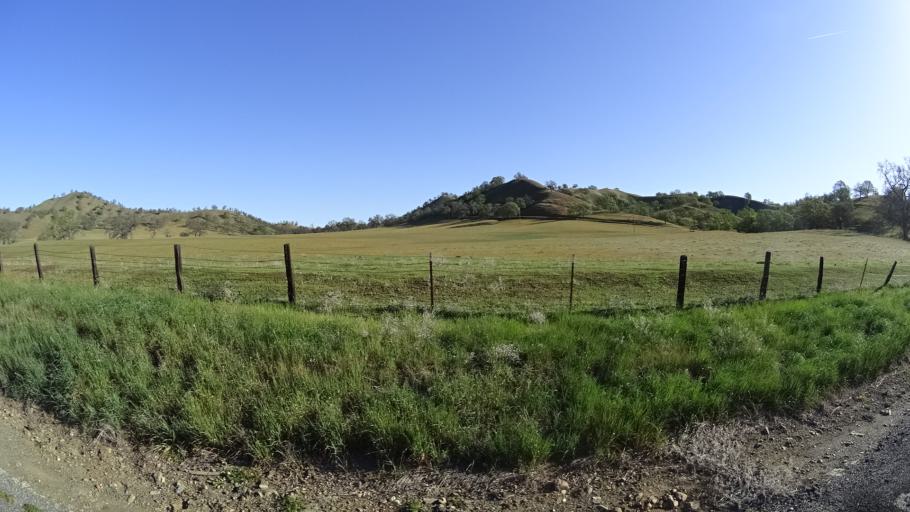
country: US
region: California
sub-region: Tehama County
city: Rancho Tehama Reserve
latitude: 39.7886
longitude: -122.4867
